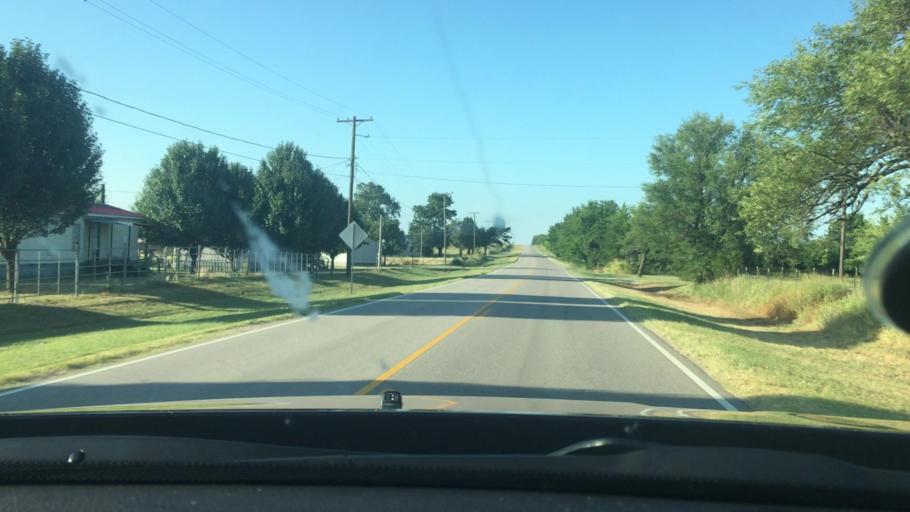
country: US
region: Oklahoma
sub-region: Murray County
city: Sulphur
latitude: 34.6150
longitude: -96.8448
